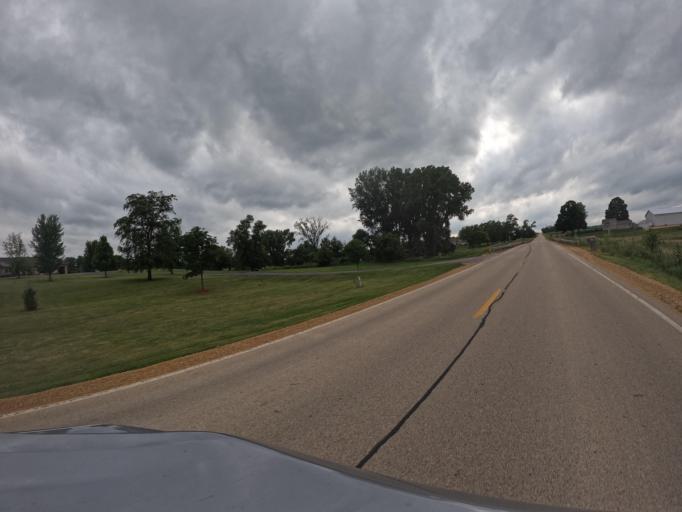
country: US
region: Iowa
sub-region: Clinton County
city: De Witt
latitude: 41.8006
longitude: -90.5159
